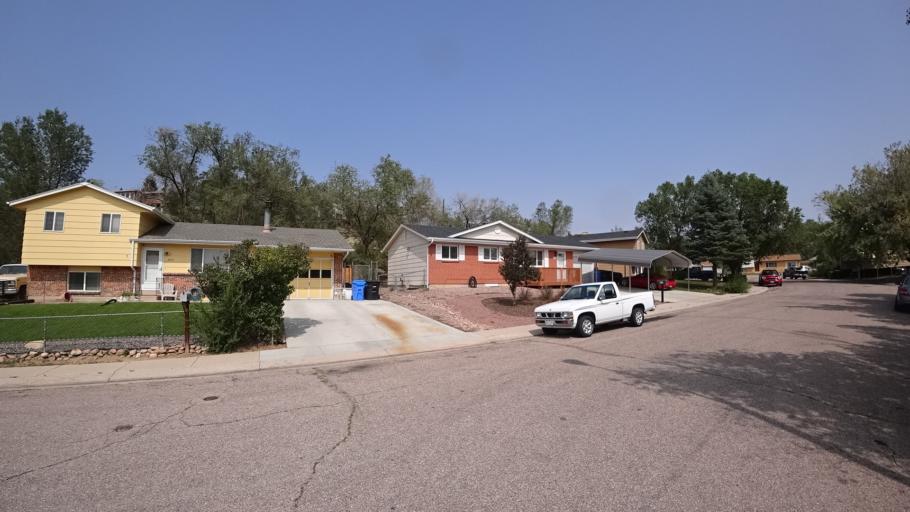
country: US
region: Colorado
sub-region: El Paso County
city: Stratmoor
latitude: 38.7986
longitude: -104.7745
